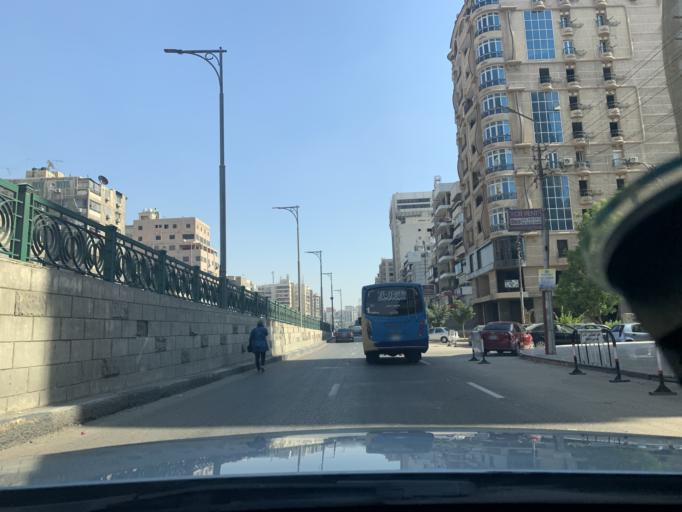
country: EG
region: Muhafazat al Qahirah
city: Cairo
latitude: 30.0806
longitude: 31.3399
